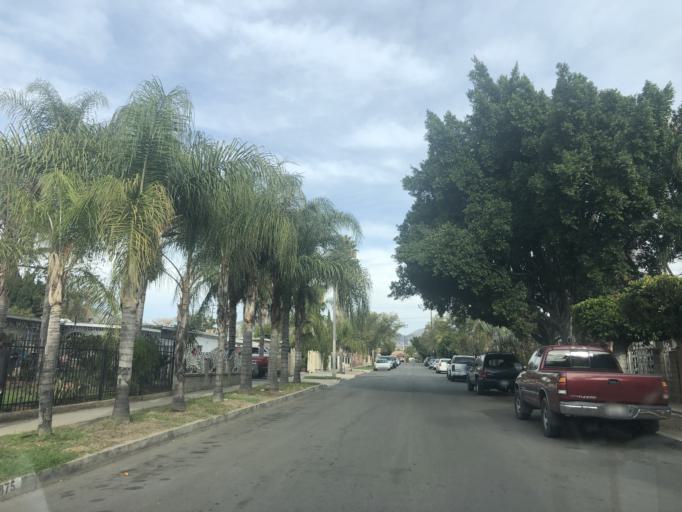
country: US
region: California
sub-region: Los Angeles County
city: San Fernando
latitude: 34.2706
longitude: -118.4354
